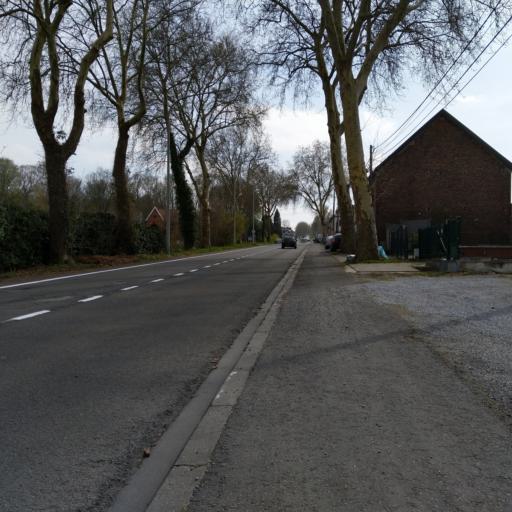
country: BE
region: Wallonia
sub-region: Province du Hainaut
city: Chasse Royale
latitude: 50.4211
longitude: 3.9499
